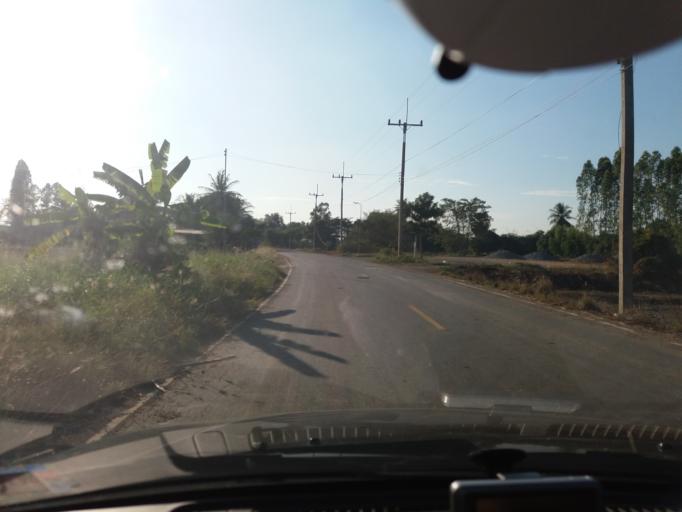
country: TH
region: Suphan Buri
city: Doem Bang Nang Buat
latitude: 14.9134
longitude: 100.1395
